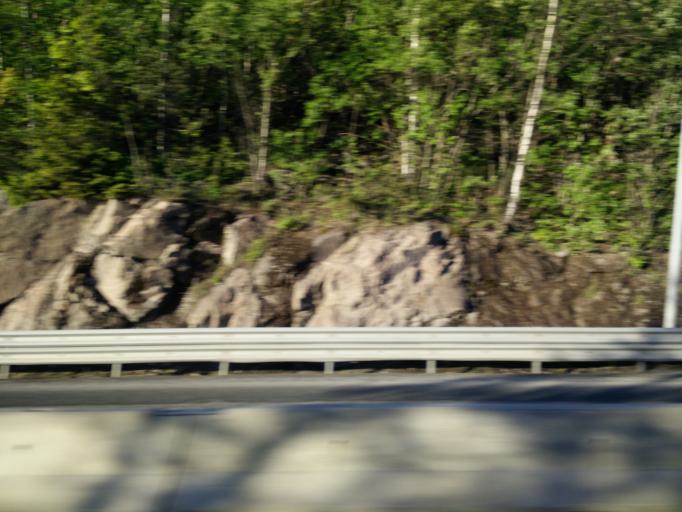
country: NO
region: Buskerud
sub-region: Hole
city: Vik
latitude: 59.9863
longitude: 10.3065
